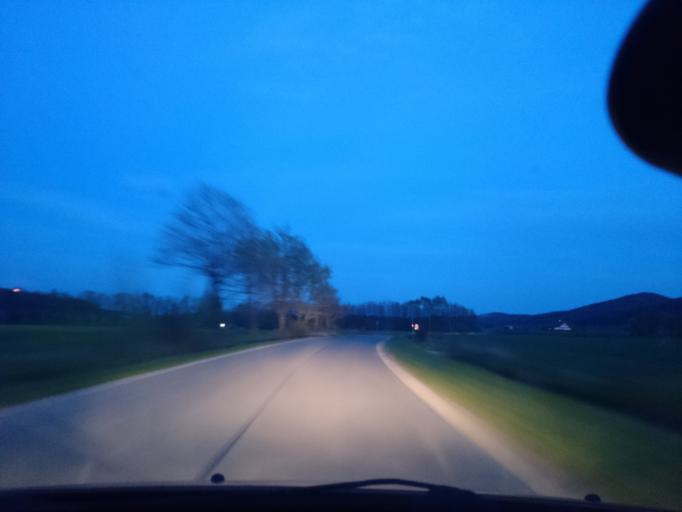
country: PL
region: Lower Silesian Voivodeship
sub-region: Powiat zabkowicki
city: Budzow
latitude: 50.5606
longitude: 16.6924
